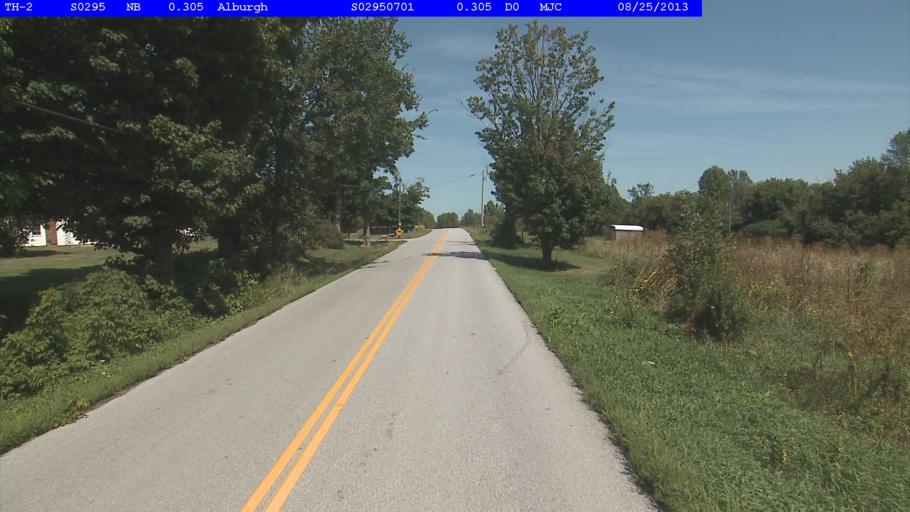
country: US
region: Vermont
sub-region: Franklin County
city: Swanton
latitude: 44.9790
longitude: -73.2302
